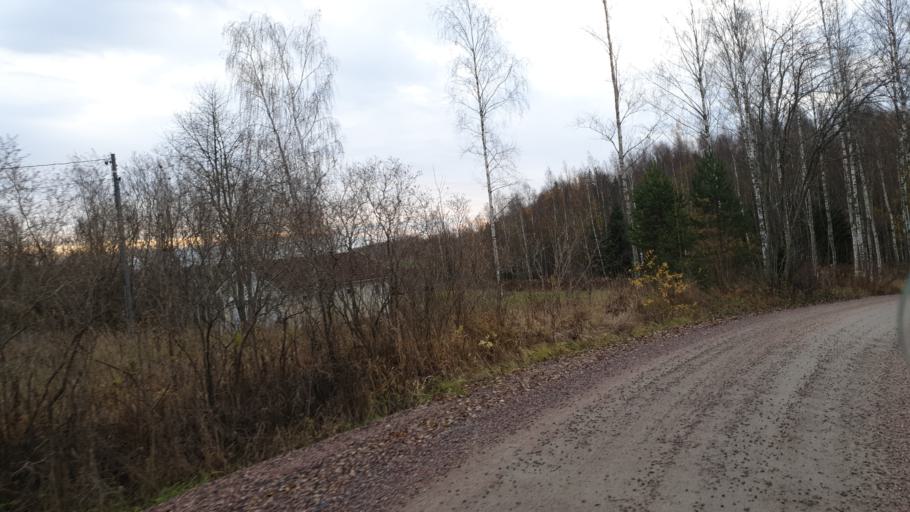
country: FI
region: Uusimaa
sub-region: Helsinki
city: Siuntio
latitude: 60.1174
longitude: 24.3006
